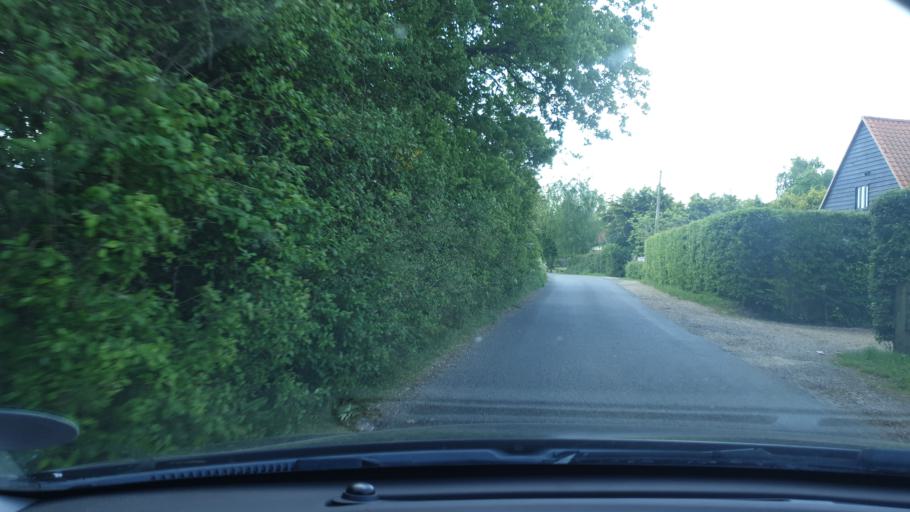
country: GB
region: England
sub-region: Essex
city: Great Bentley
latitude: 51.8457
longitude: 1.0905
